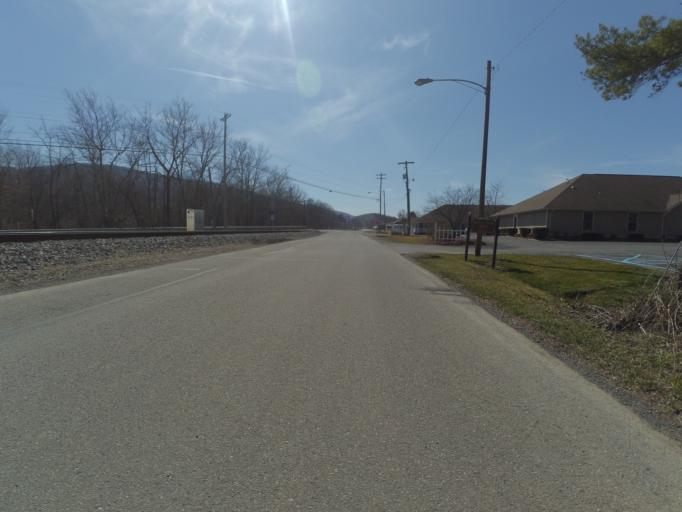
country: US
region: Pennsylvania
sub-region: Centre County
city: Milesburg
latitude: 40.9427
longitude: -77.7960
